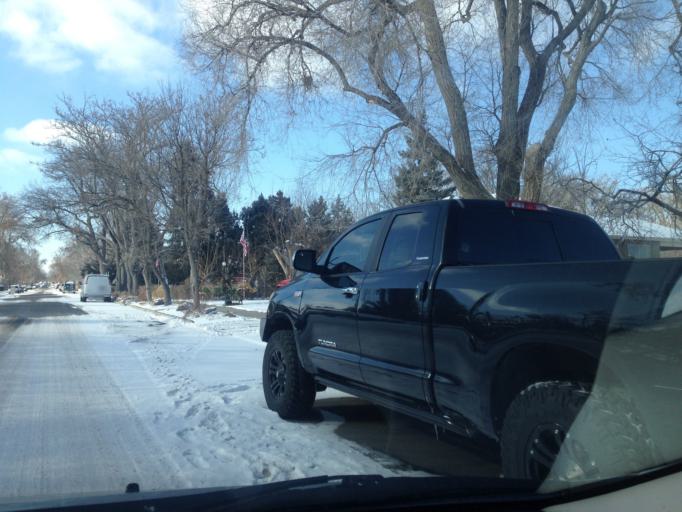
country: US
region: Colorado
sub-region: Boulder County
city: Lafayette
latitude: 39.9983
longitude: -105.0816
